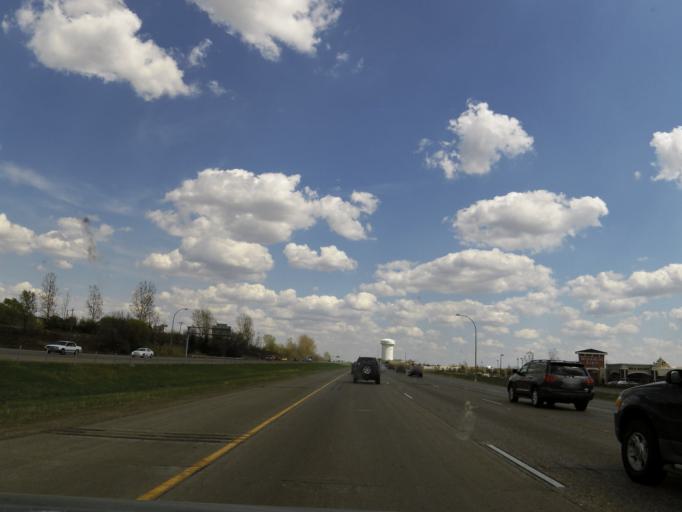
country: US
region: Minnesota
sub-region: Washington County
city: Oakdale
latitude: 44.9487
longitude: -92.9283
